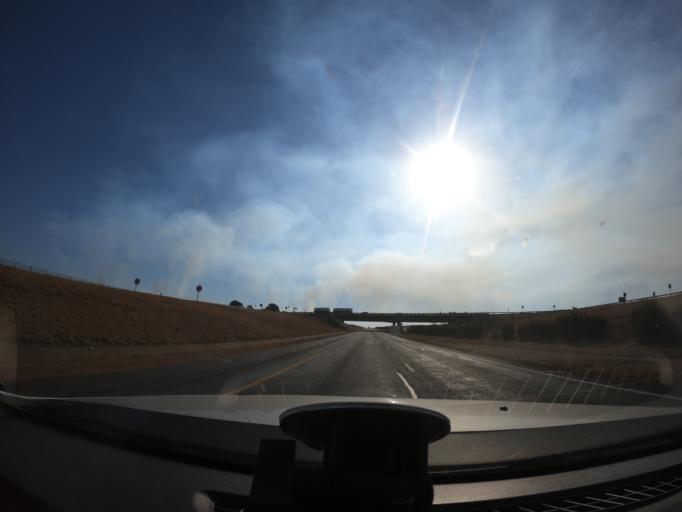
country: ZA
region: Gauteng
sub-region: Sedibeng District Municipality
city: Heidelberg
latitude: -26.4920
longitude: 28.3744
